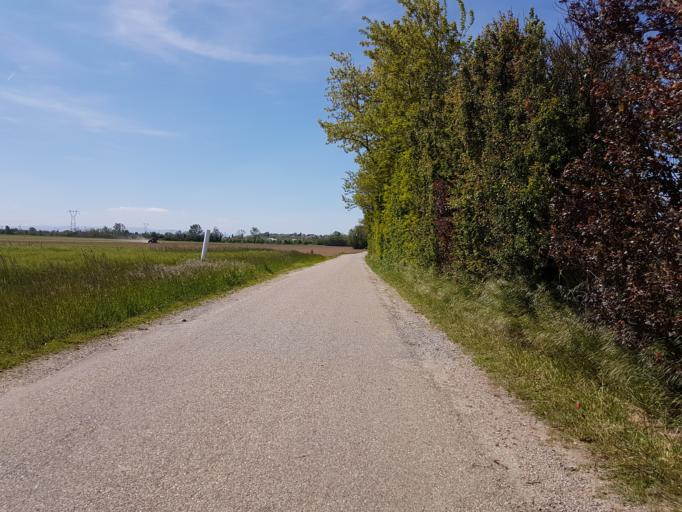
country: FR
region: Rhone-Alpes
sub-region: Departement du Rhone
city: Jons
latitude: 45.7900
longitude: 5.0678
